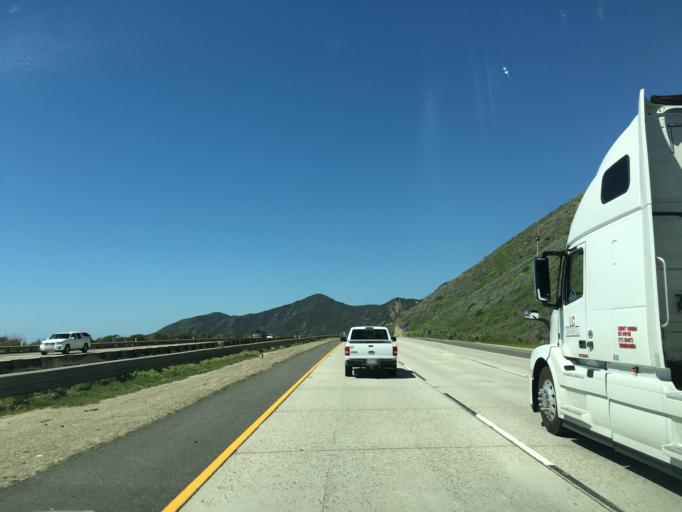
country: US
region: California
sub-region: Ventura County
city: Ventura
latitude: 34.3127
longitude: -119.3576
